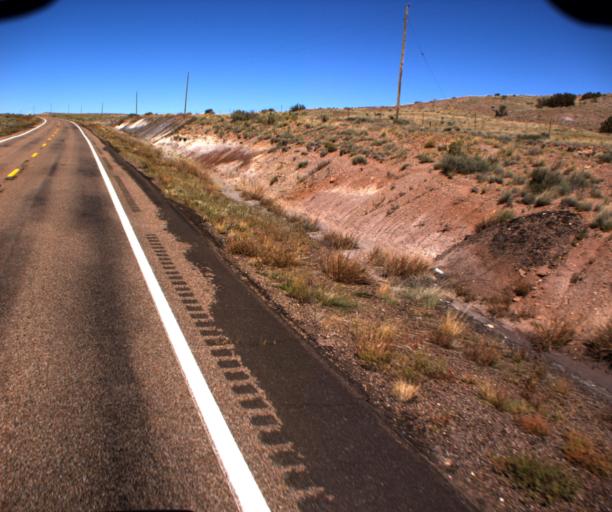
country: US
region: Arizona
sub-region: Apache County
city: Saint Johns
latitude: 34.5270
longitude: -109.4570
